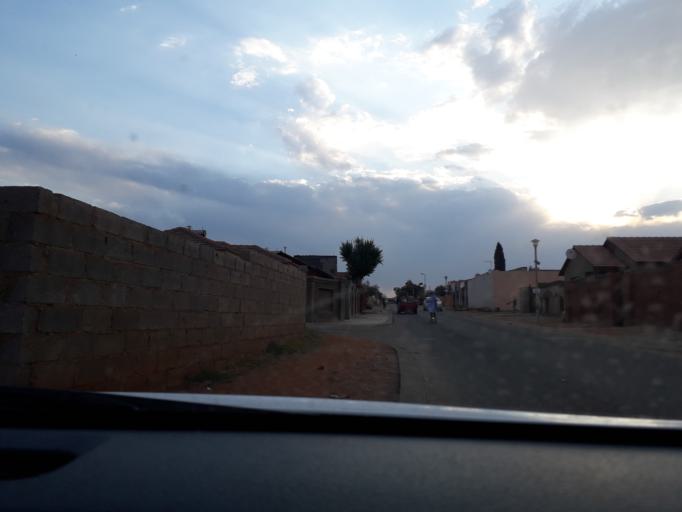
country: ZA
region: Gauteng
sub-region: City of Johannesburg Metropolitan Municipality
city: Midrand
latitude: -26.0109
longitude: 28.1730
